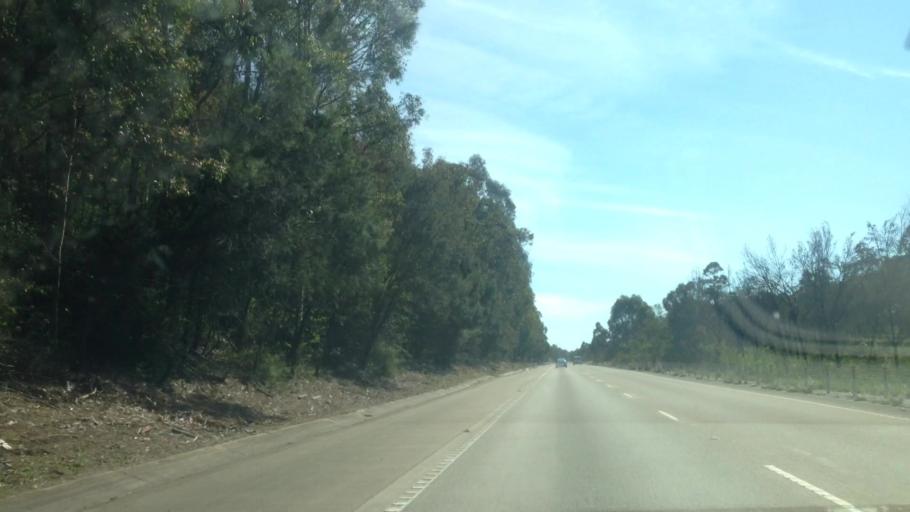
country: AU
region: New South Wales
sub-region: Lake Macquarie Shire
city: Fennell Bay
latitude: -32.9687
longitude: 151.5350
